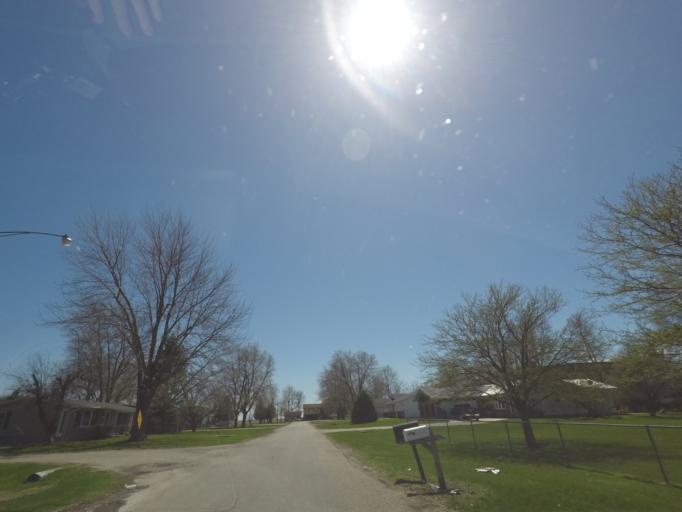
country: US
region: Illinois
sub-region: Macon County
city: Warrensburg
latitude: 39.9679
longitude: -89.1568
